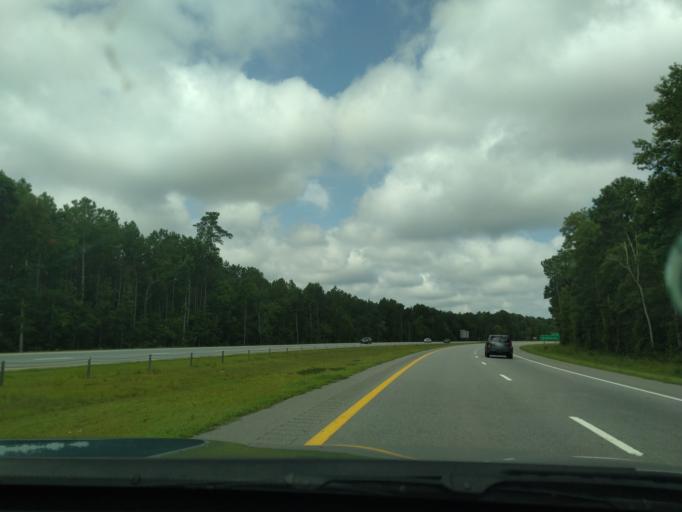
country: US
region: North Carolina
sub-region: Martin County
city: Williamston
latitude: 35.8177
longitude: -77.0924
